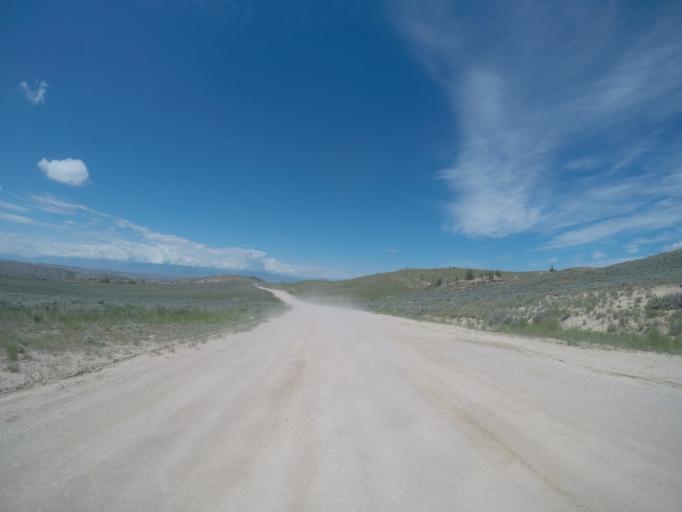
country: US
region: Wyoming
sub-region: Park County
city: Powell
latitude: 45.2066
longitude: -108.7836
